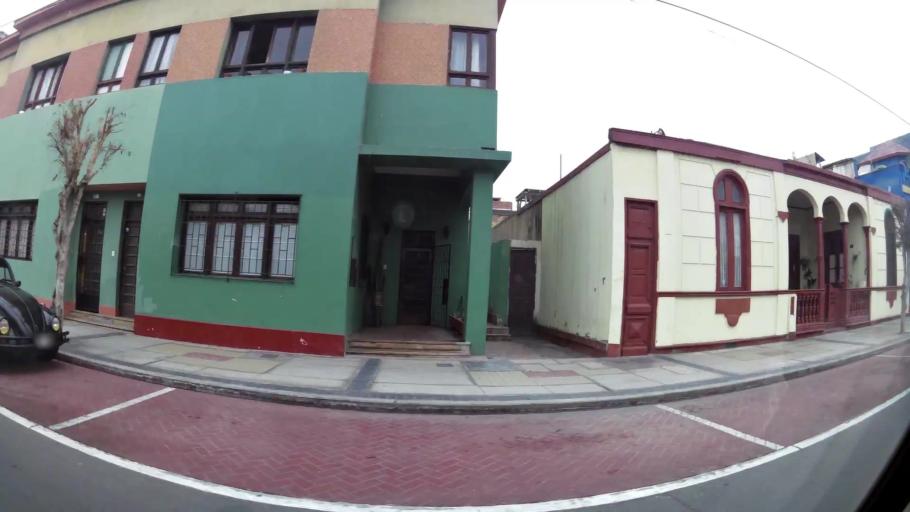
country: PE
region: Callao
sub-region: Callao
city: Callao
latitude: -12.0717
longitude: -77.1625
